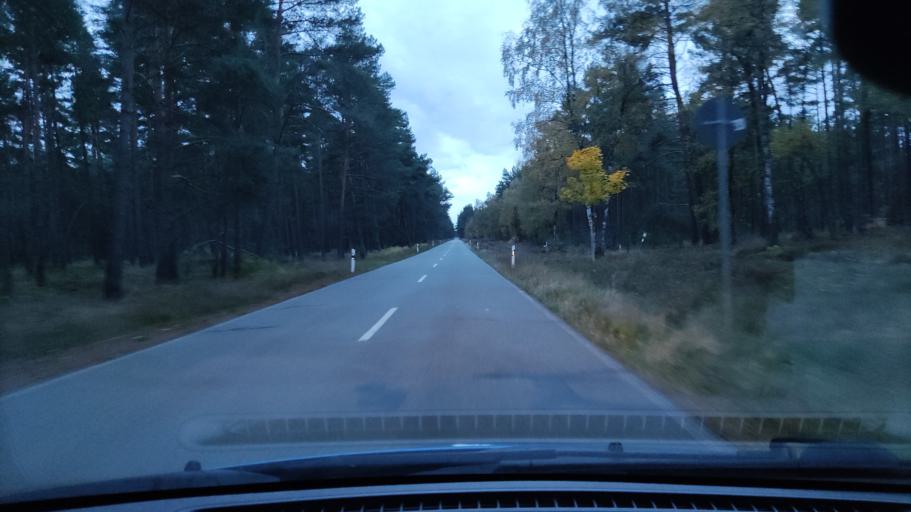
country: DE
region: Lower Saxony
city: Prezelle
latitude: 53.0087
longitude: 11.3901
